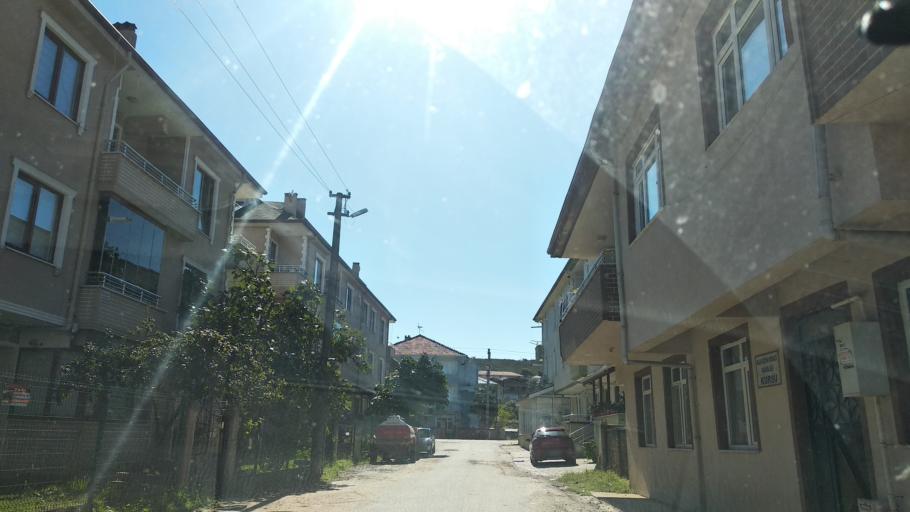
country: TR
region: Sakarya
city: Karasu
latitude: 41.0912
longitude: 30.7031
